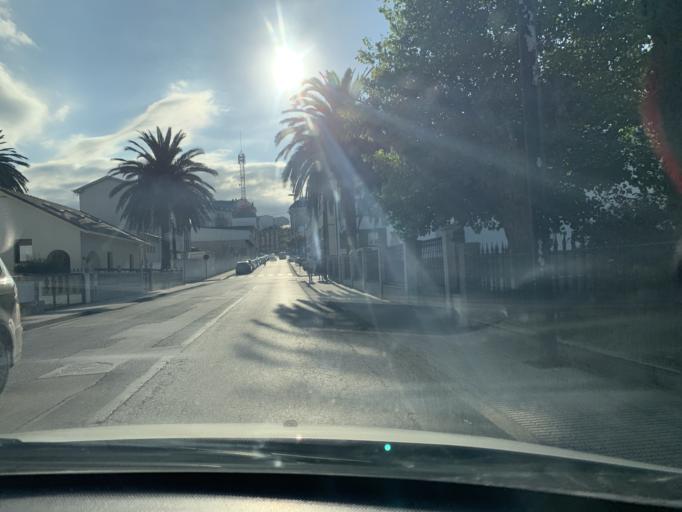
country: ES
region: Galicia
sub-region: Provincia de Lugo
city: Foz
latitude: 43.5696
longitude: -7.2550
